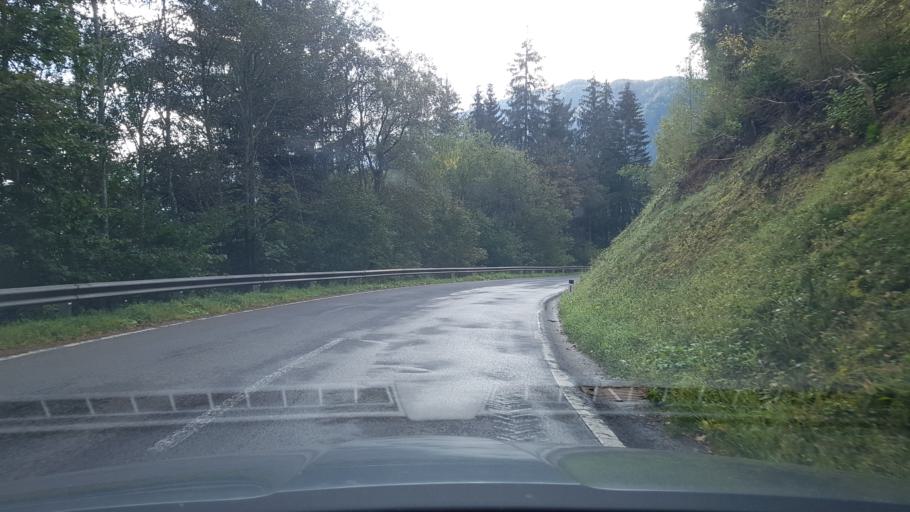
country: AT
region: Styria
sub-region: Politischer Bezirk Murau
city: Schoder
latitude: 47.1949
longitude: 14.1207
